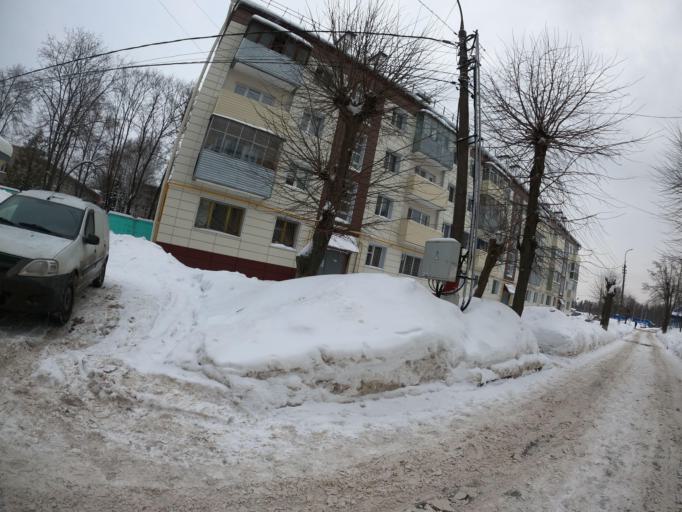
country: RU
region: Moskovskaya
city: Elektrogorsk
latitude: 55.8673
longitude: 38.7814
